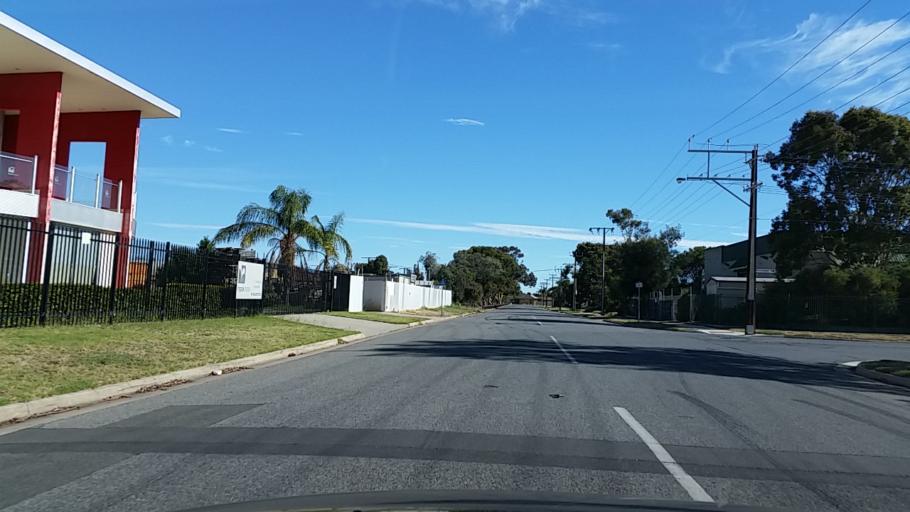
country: AU
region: South Australia
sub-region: Port Adelaide Enfield
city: Cheltenham
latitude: -34.8652
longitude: 138.5073
